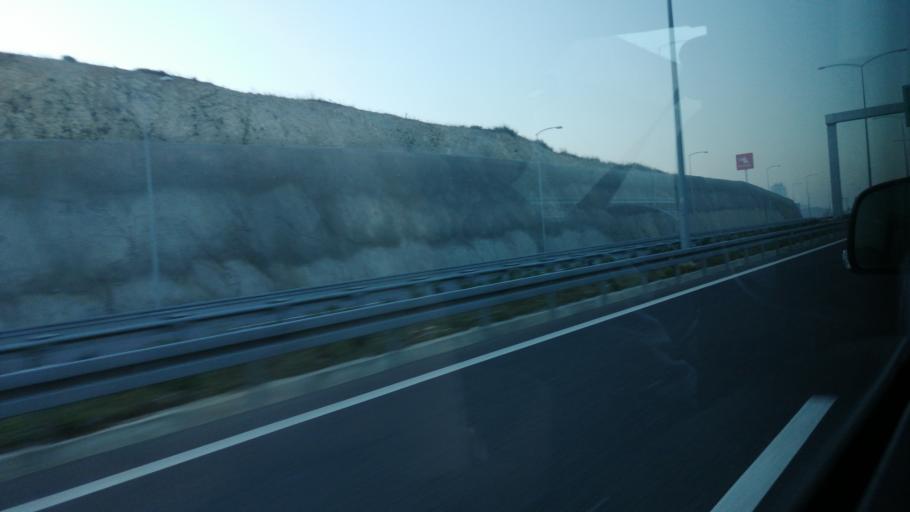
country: TR
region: Kocaeli
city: Tavsanli
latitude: 40.7788
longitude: 29.5180
